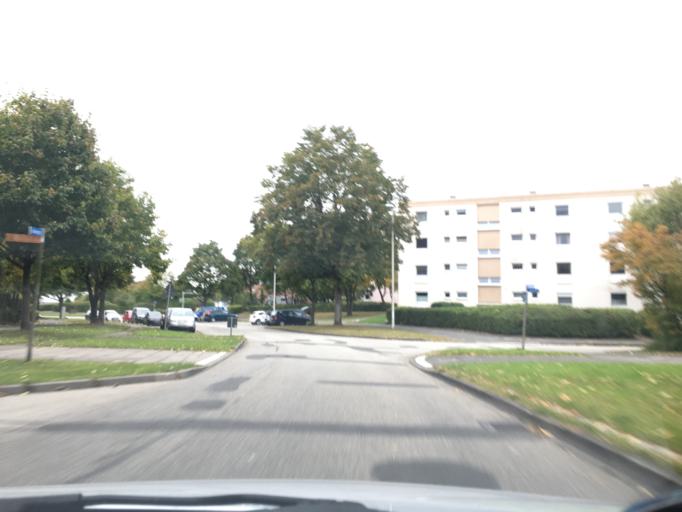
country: DE
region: Schleswig-Holstein
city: Melsdorf
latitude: 54.3197
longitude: 10.0480
